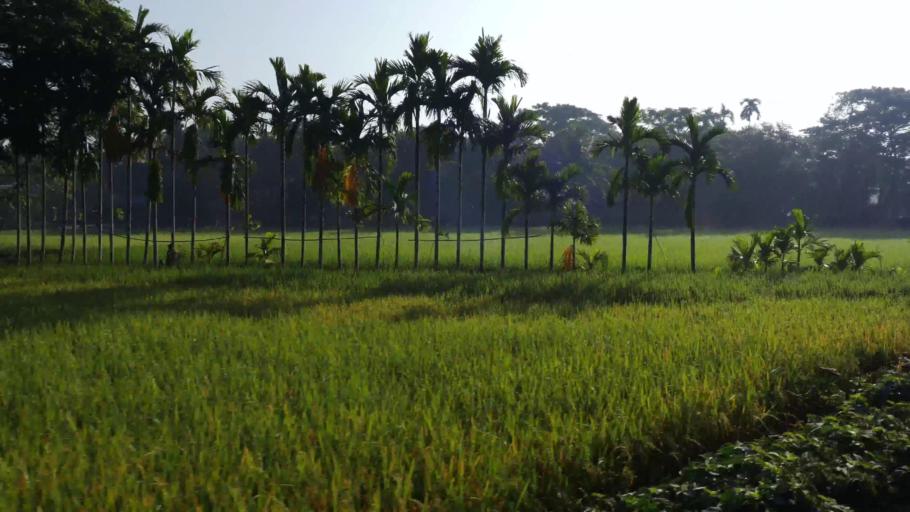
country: BD
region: Dhaka
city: Jamalpur
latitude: 24.8633
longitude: 90.0629
